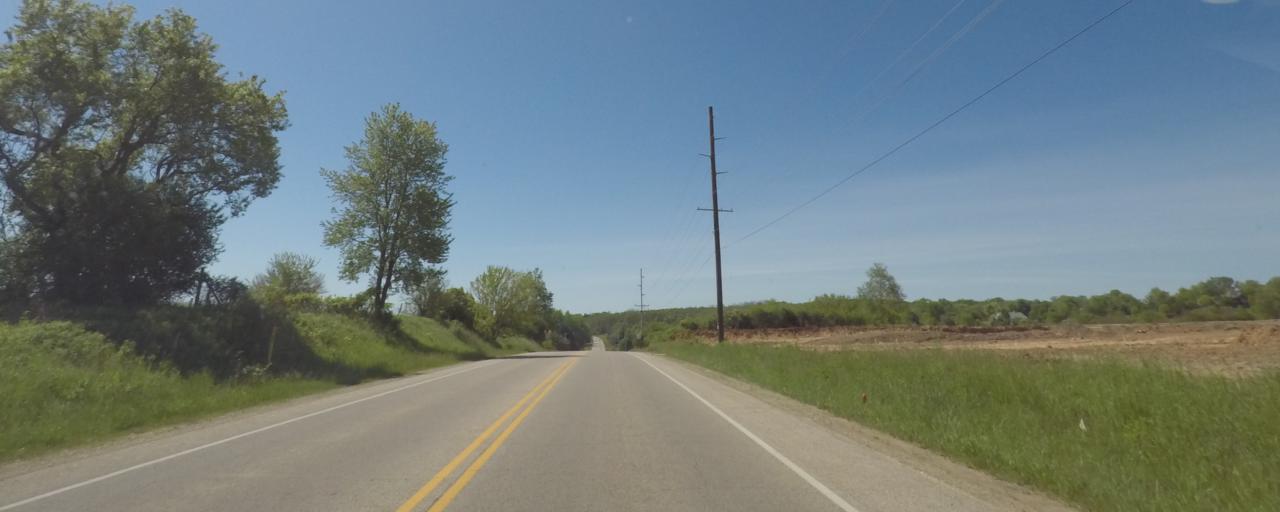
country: US
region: Wisconsin
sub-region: Dane County
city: Oregon
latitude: 42.9081
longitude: -89.3739
